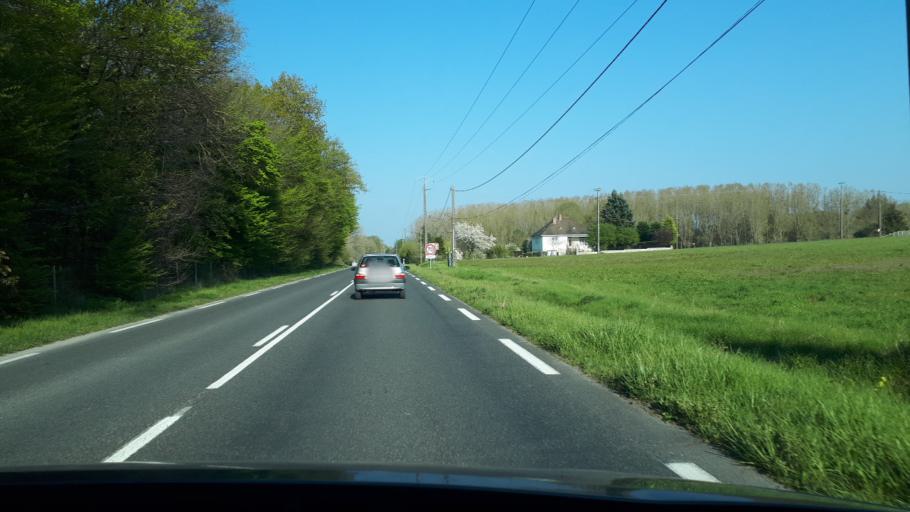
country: FR
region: Centre
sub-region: Departement d'Indre-et-Loire
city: Civray-de-Touraine
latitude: 47.3215
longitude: 1.0766
